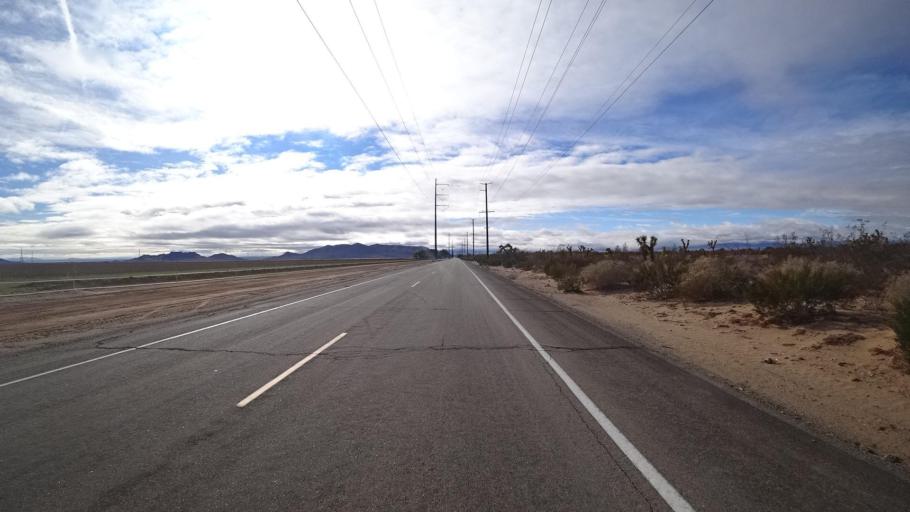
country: US
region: California
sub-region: Kern County
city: Rosamond
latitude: 34.9285
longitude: -118.2916
